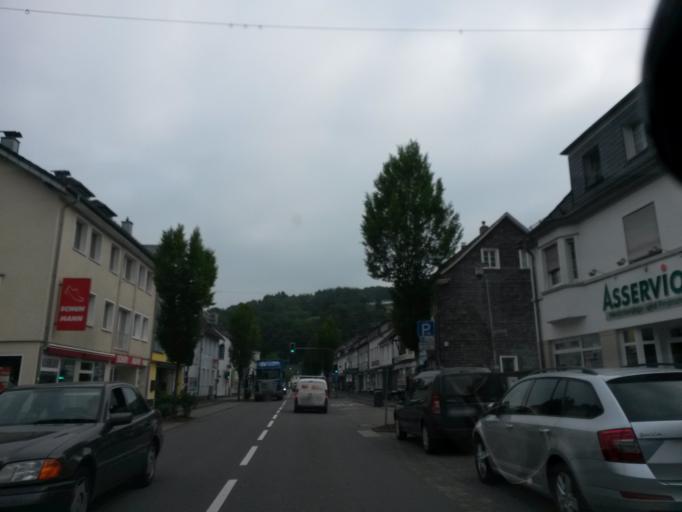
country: DE
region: North Rhine-Westphalia
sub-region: Regierungsbezirk Koln
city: Engelskirchen
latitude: 50.9856
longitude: 7.4094
